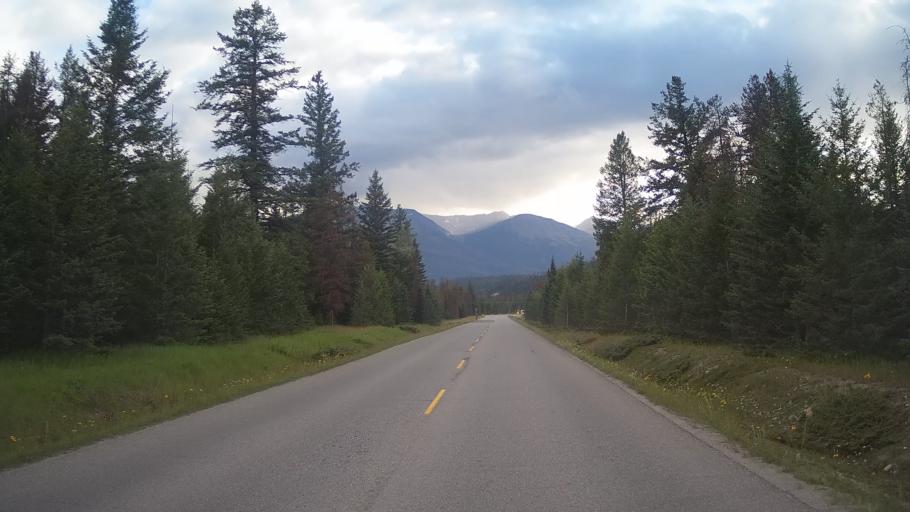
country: CA
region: Alberta
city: Jasper Park Lodge
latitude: 52.9126
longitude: -118.0511
